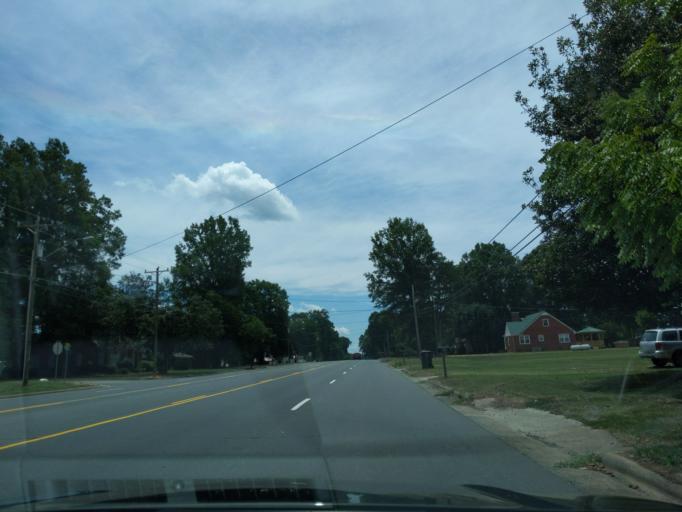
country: US
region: North Carolina
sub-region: Stanly County
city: Albemarle
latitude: 35.4223
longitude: -80.2108
